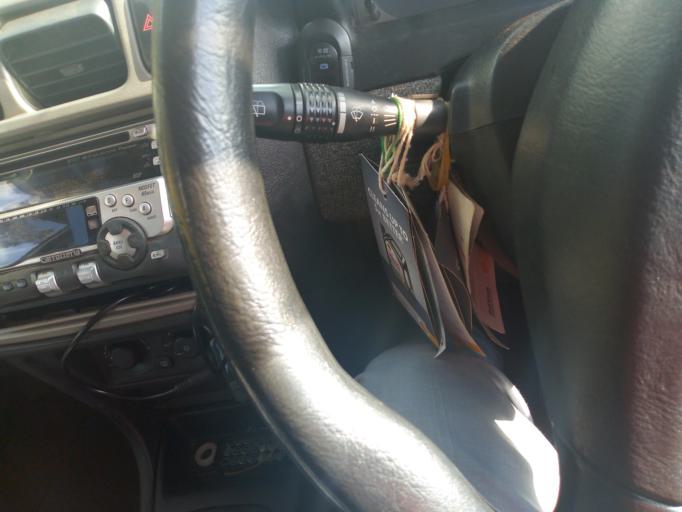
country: UG
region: Western Region
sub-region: Masindi District
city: Masindi
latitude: 1.6555
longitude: 31.7062
